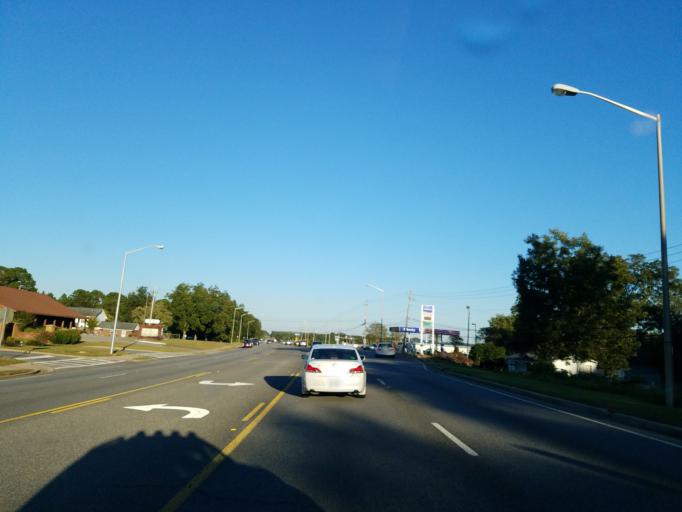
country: US
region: Georgia
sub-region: Worth County
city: Sylvester
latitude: 31.5274
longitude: -83.8177
